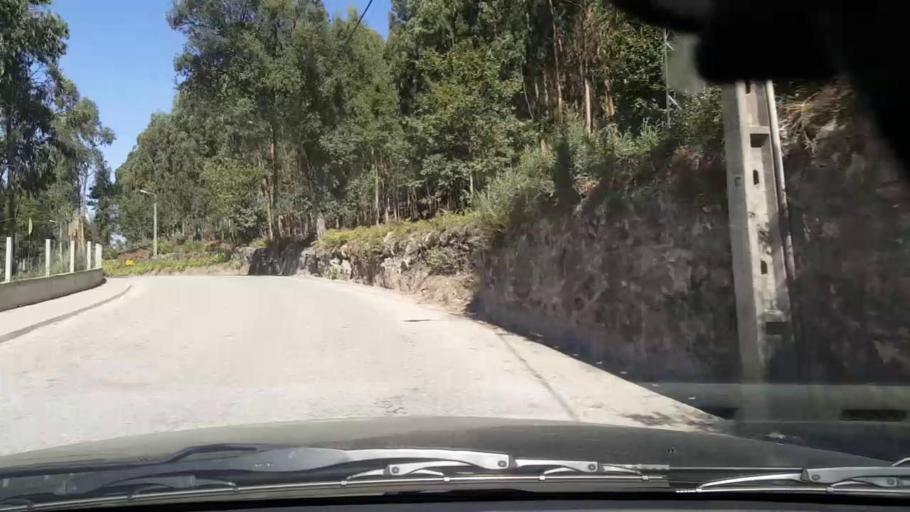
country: PT
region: Porto
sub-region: Maia
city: Gemunde
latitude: 41.3236
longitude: -8.6410
